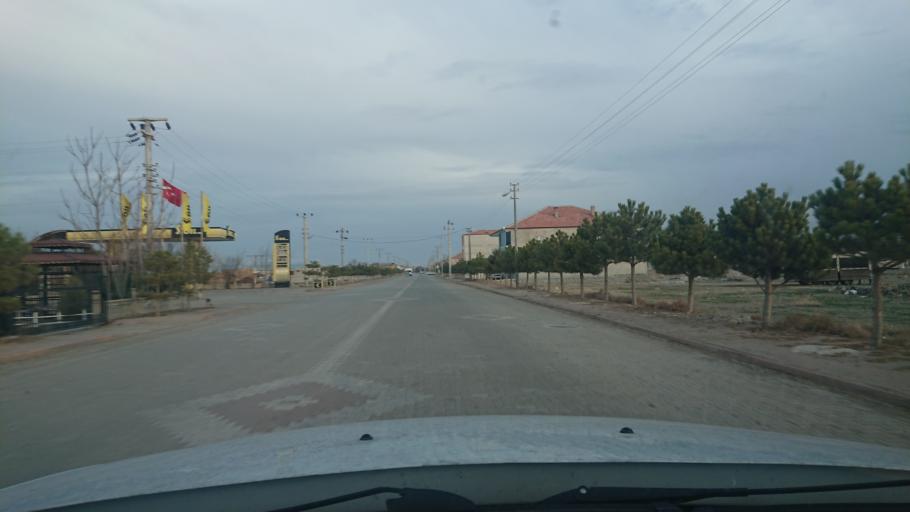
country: TR
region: Aksaray
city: Yesilova
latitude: 38.3351
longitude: 33.7514
